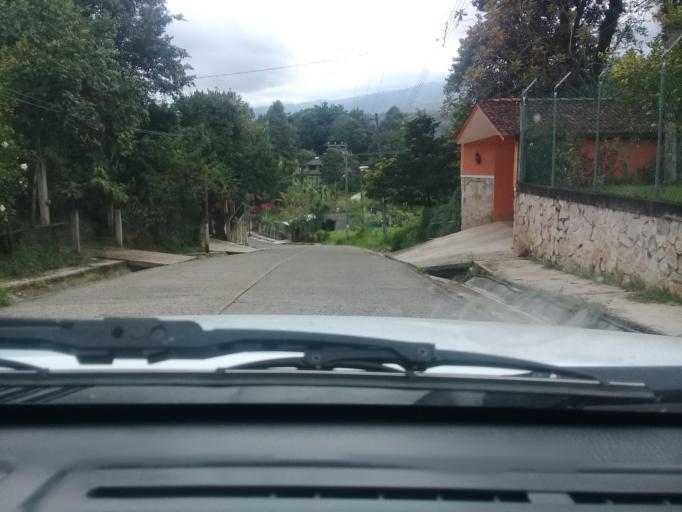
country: MX
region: Veracruz
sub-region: Tlalnelhuayocan
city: Guadalupe Victoria
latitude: 19.5442
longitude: -96.9672
